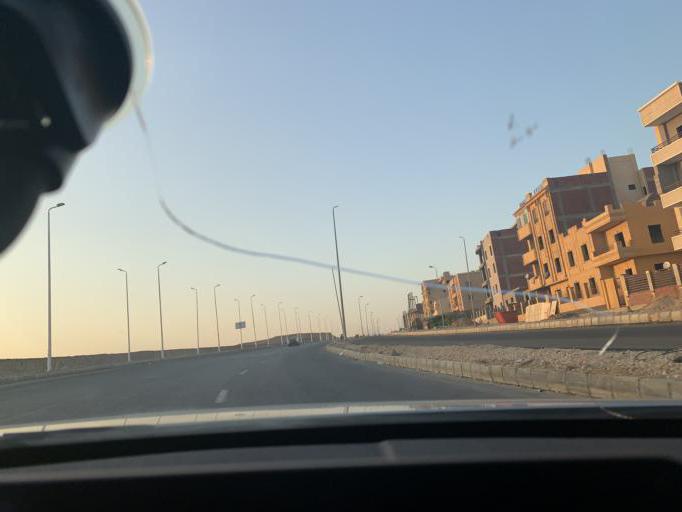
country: EG
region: Muhafazat al Qahirah
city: Halwan
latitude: 29.9782
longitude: 31.4691
